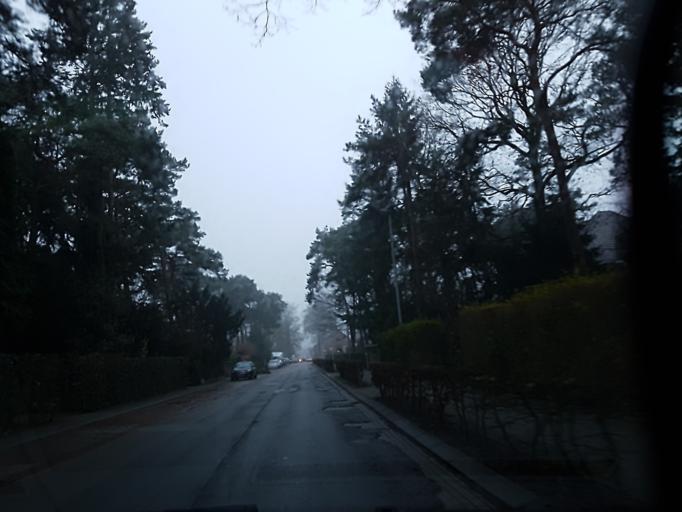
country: BE
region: Flanders
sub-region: Provincie Vlaams-Brabant
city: Boortmeerbeek
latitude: 51.0057
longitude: 4.5908
